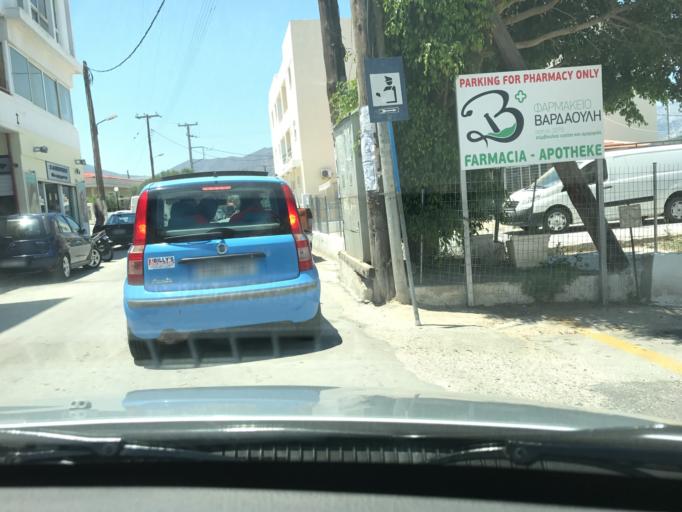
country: GR
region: South Aegean
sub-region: Nomos Dodekanisou
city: Karpathos
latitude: 35.5071
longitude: 27.2108
